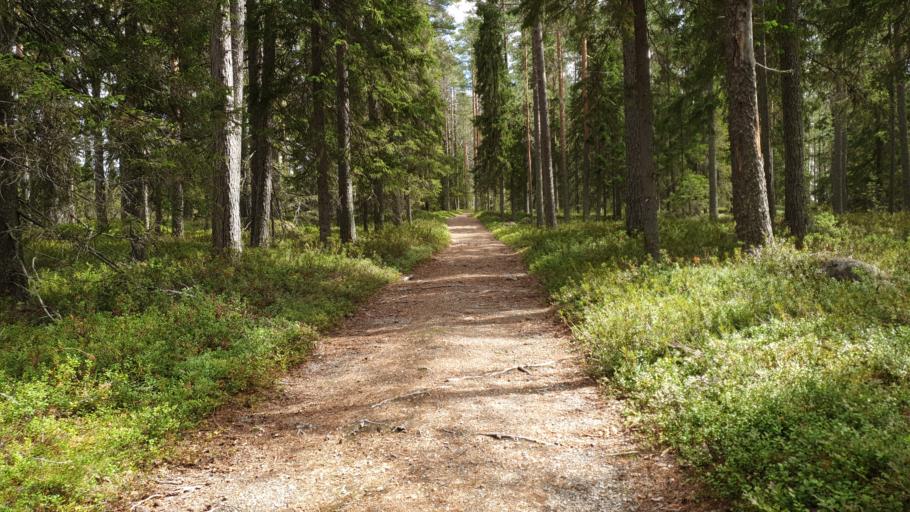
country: FI
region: Kainuu
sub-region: Kehys-Kainuu
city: Kuhmo
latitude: 64.3822
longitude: 29.8037
